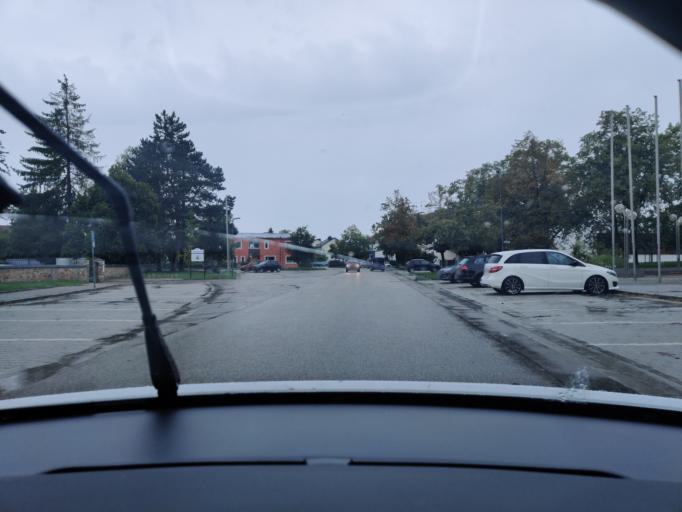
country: DE
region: Bavaria
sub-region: Upper Palatinate
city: Schwarzenfeld
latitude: 49.3889
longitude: 12.1358
